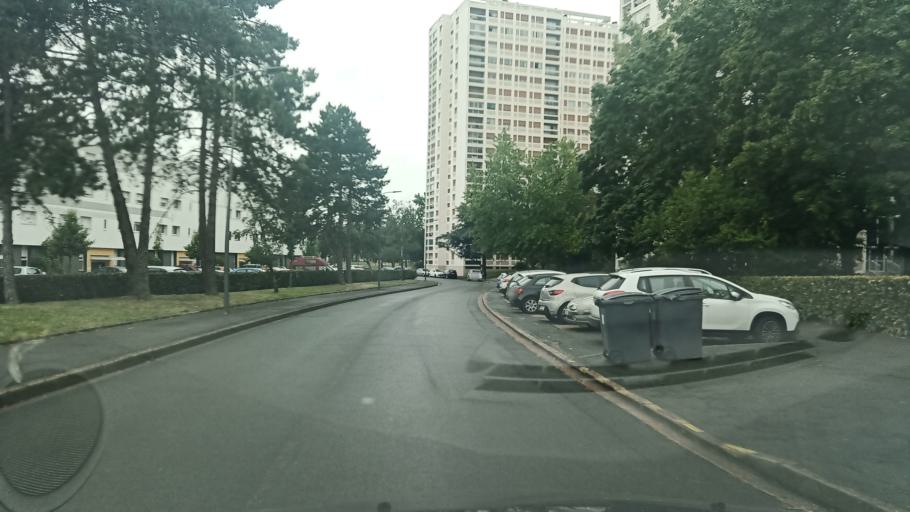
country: FR
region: Poitou-Charentes
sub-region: Departement de la Vienne
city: Poitiers
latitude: 46.5881
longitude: 0.3579
